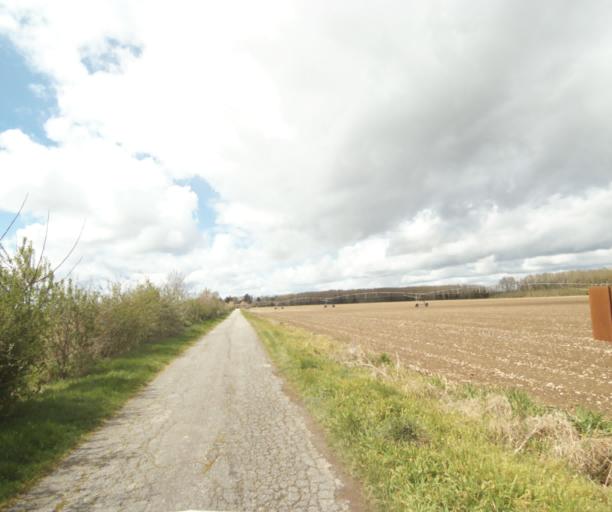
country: FR
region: Midi-Pyrenees
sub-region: Departement de la Haute-Garonne
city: Calmont
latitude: 43.2542
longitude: 1.6329
